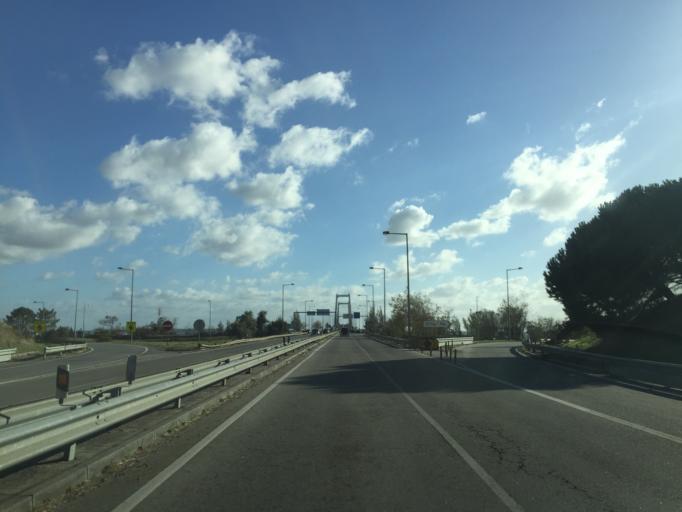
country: PT
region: Coimbra
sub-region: Figueira da Foz
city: Tavarede
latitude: 40.1540
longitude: -8.8416
